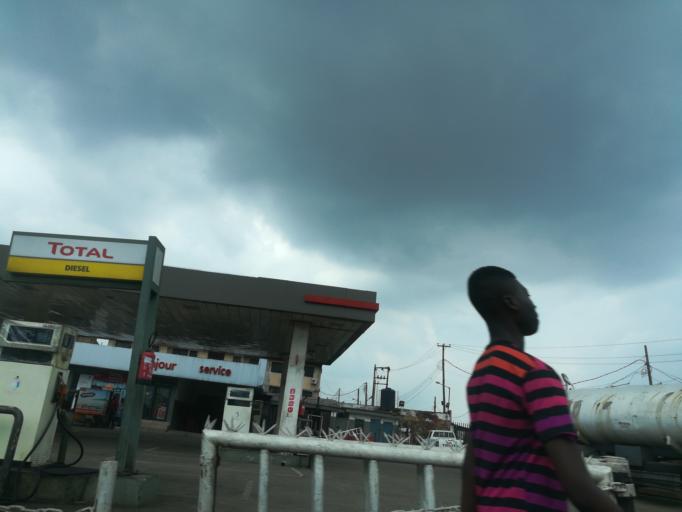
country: NG
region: Lagos
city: Ojota
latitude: 6.5911
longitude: 3.3740
